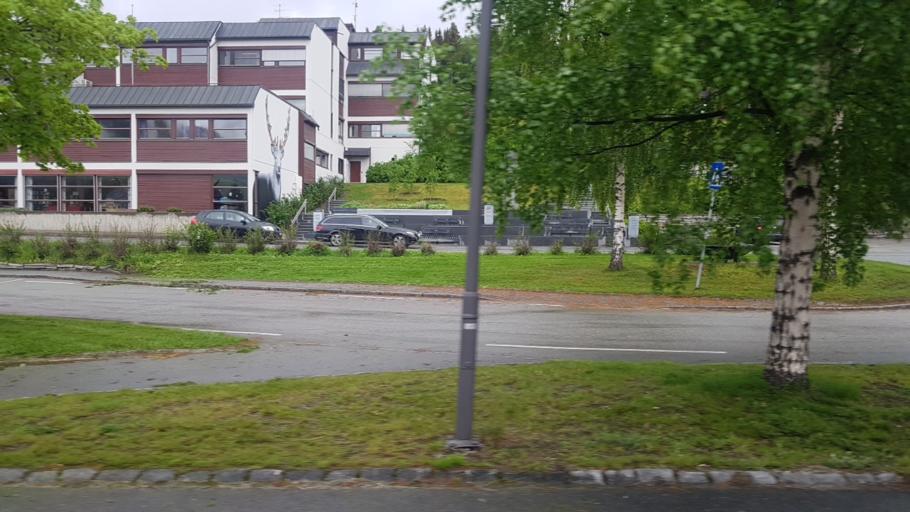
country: NO
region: Oppland
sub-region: Nord-Fron
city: Vinstra
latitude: 61.5978
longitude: 9.7341
